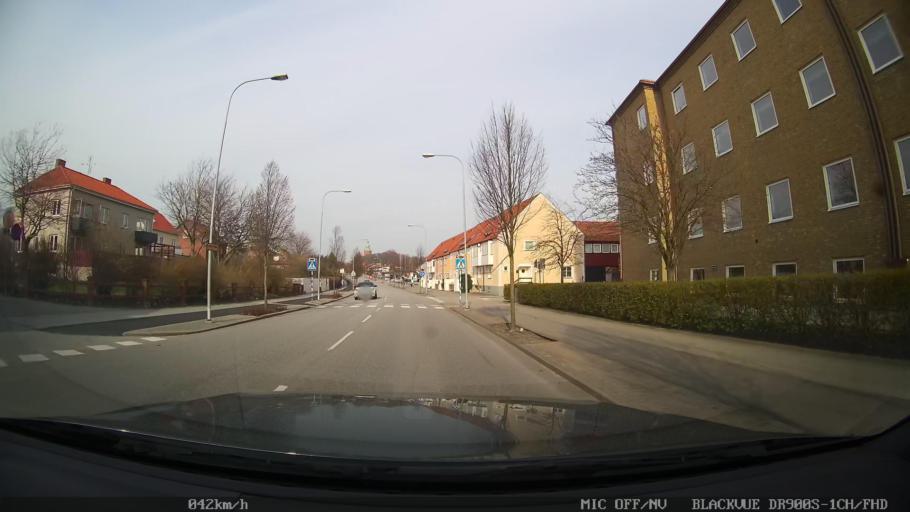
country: SE
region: Skane
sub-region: Ystads Kommun
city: Ystad
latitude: 55.4336
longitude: 13.8200
